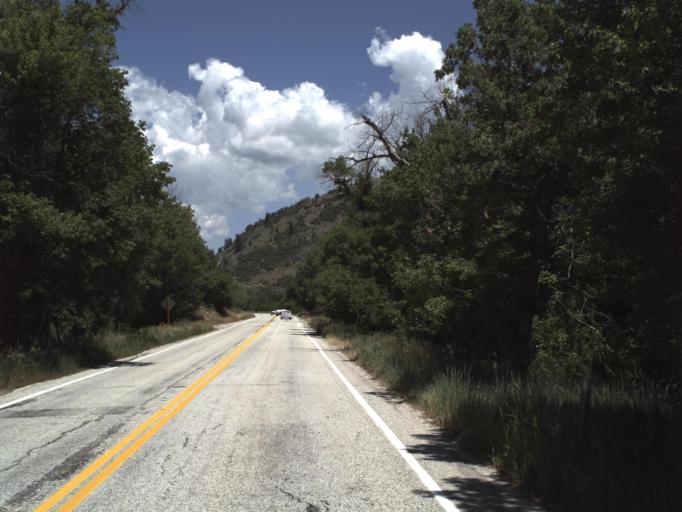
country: US
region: Utah
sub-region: Weber County
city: Wolf Creek
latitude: 41.2699
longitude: -111.6688
